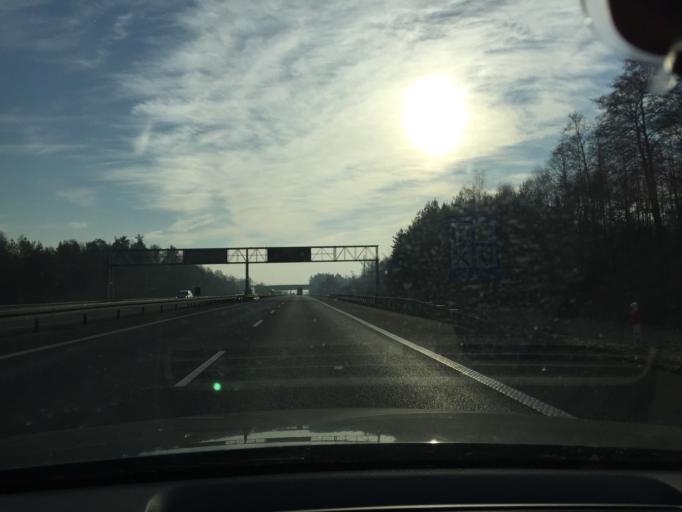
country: PL
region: Silesian Voivodeship
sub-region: Powiat gliwicki
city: Sosnicowice
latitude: 50.3350
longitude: 18.5448
